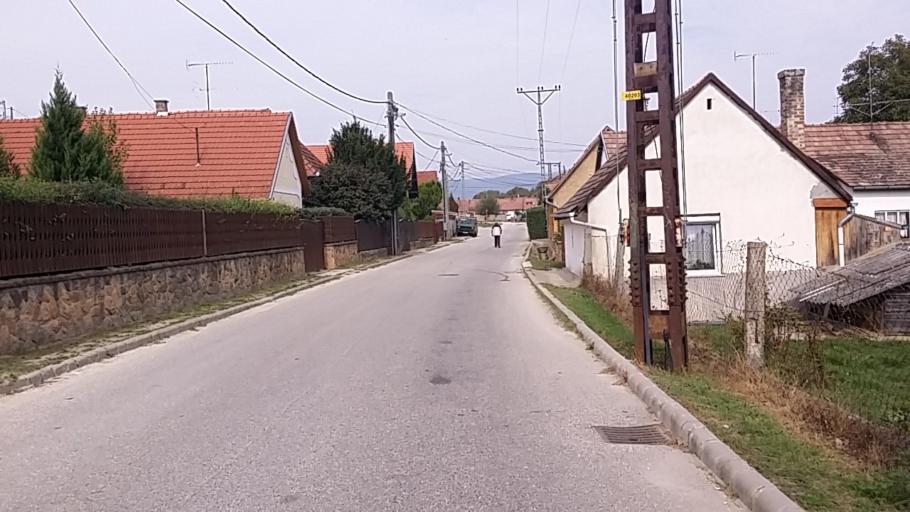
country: HU
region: Pest
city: Csobanka
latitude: 47.6452
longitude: 18.9604
